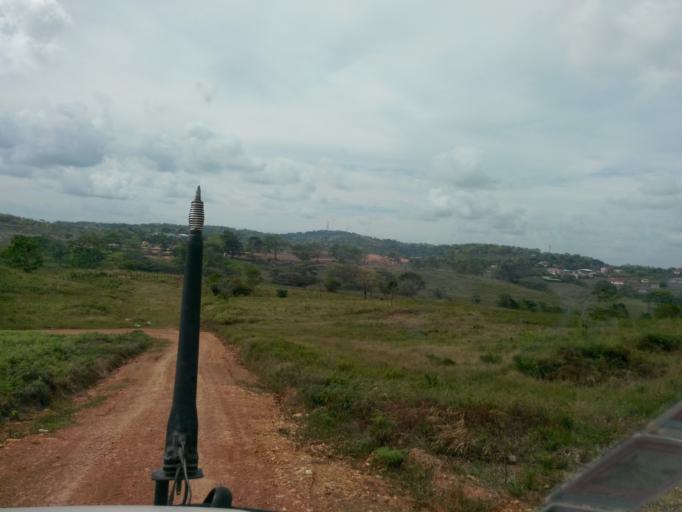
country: NI
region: Atlantico Sur
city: Bluefields
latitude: 11.9958
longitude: -83.7732
